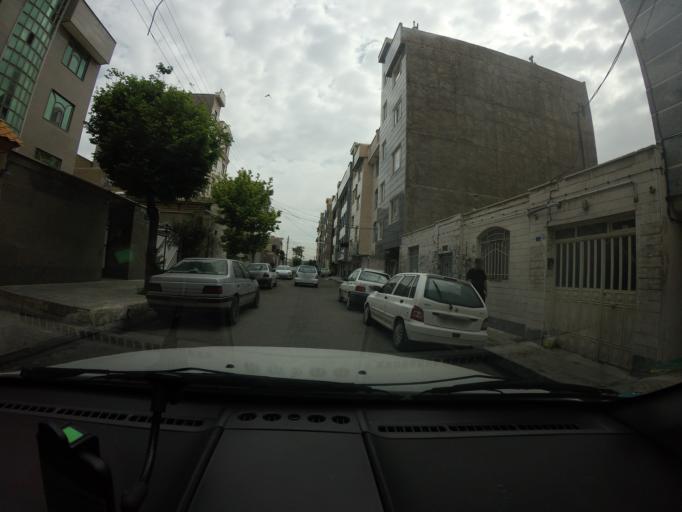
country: IR
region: Tehran
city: Eslamshahr
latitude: 35.5576
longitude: 51.2474
